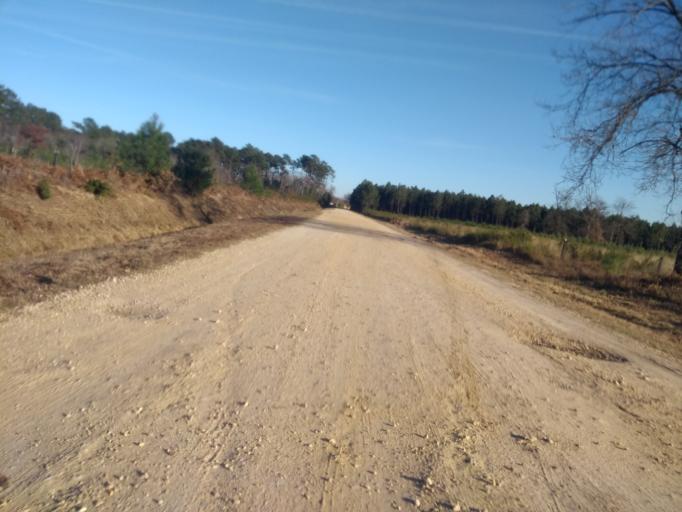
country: FR
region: Aquitaine
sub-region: Departement de la Gironde
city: Le Barp
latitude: 44.6138
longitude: -0.7851
